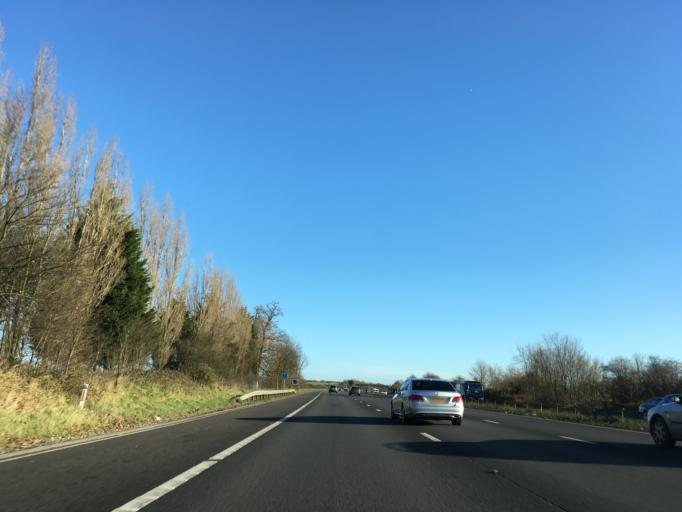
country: GB
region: England
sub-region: Wiltshire
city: Lyneham
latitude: 51.5411
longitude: -1.9821
